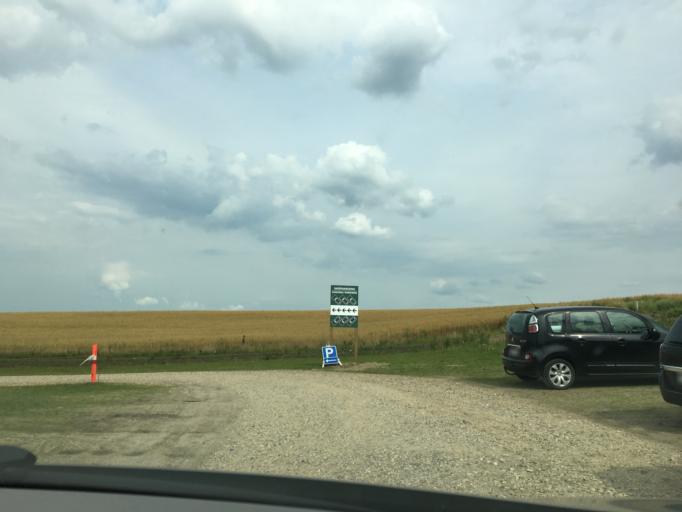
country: DK
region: Central Jutland
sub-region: Viborg Kommune
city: Stoholm
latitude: 56.4573
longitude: 9.1677
